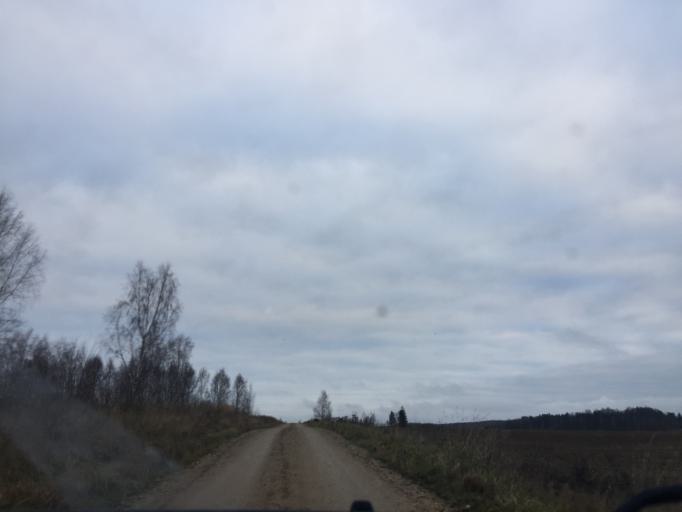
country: LV
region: Krimulda
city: Ragana
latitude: 57.1608
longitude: 24.7573
